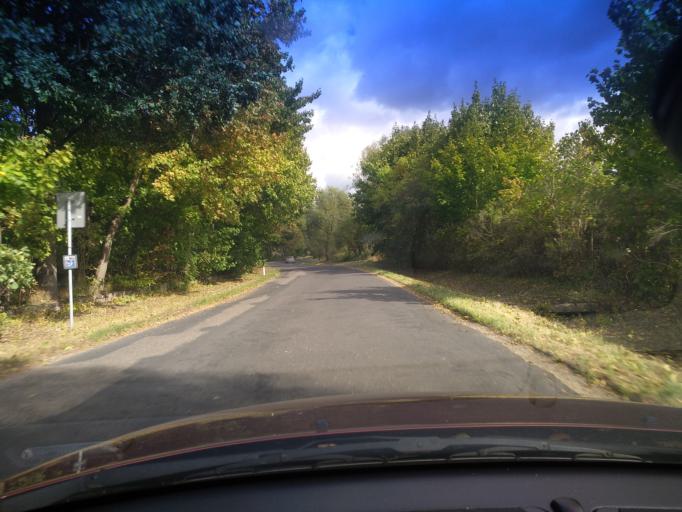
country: PL
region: Lower Silesian Voivodeship
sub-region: Powiat zgorzelecki
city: Zgorzelec
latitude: 51.1701
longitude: 15.0076
